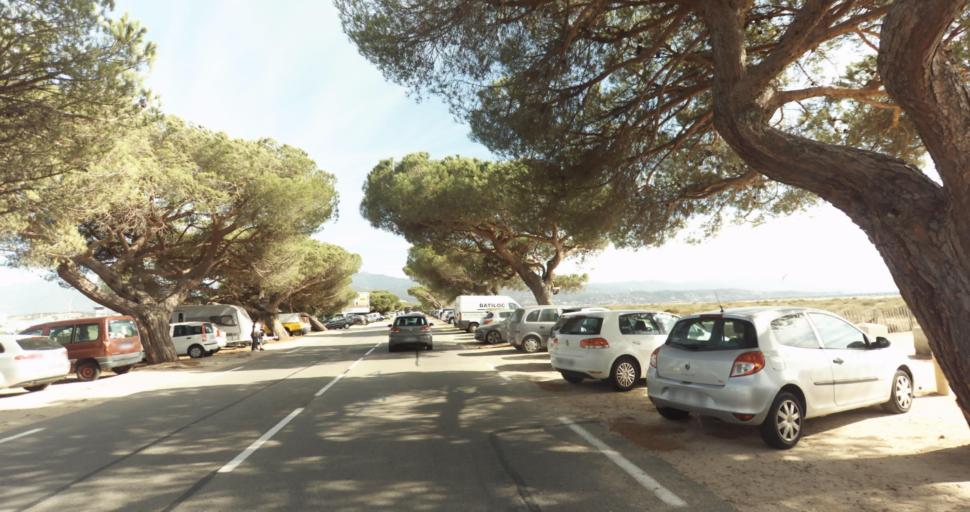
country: FR
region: Corsica
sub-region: Departement de la Corse-du-Sud
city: Ajaccio
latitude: 41.9230
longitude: 8.7850
